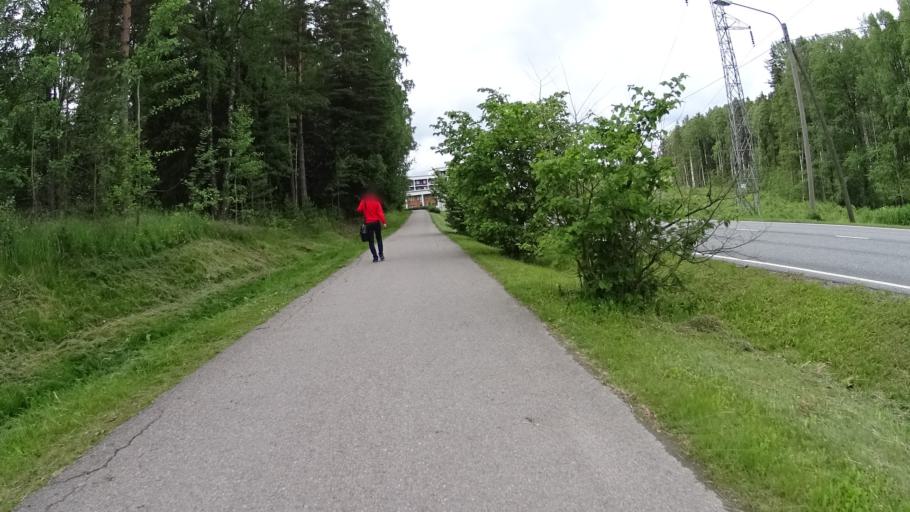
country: FI
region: Uusimaa
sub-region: Helsinki
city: Kilo
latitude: 60.2520
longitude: 24.7991
